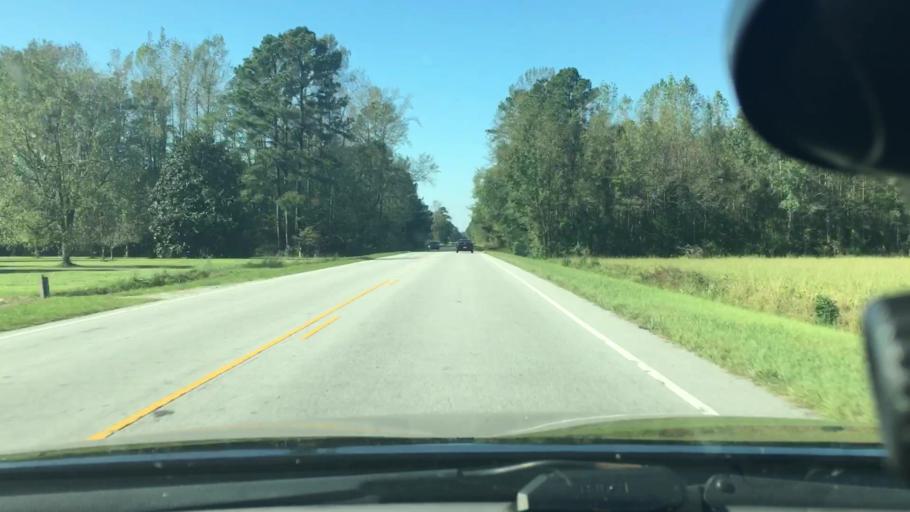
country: US
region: North Carolina
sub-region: Craven County
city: Vanceboro
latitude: 35.3025
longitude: -77.1333
